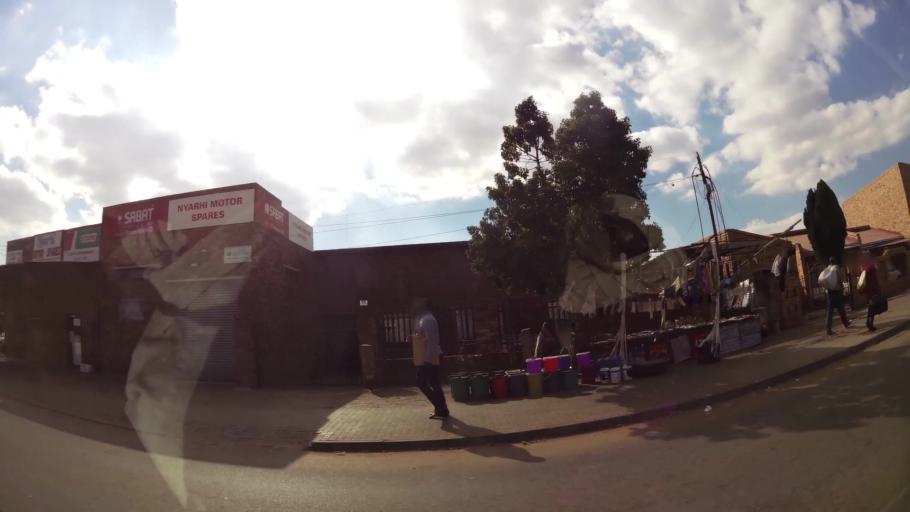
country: ZA
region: Gauteng
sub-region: Ekurhuleni Metropolitan Municipality
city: Tembisa
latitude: -26.0051
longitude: 28.2451
